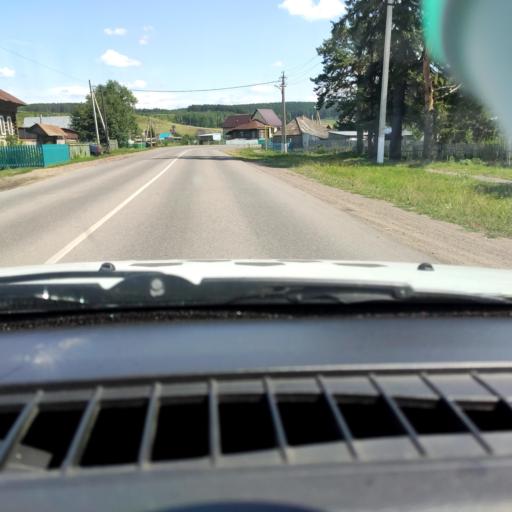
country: RU
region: Bashkortostan
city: Mesyagutovo
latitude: 55.5297
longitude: 58.2733
